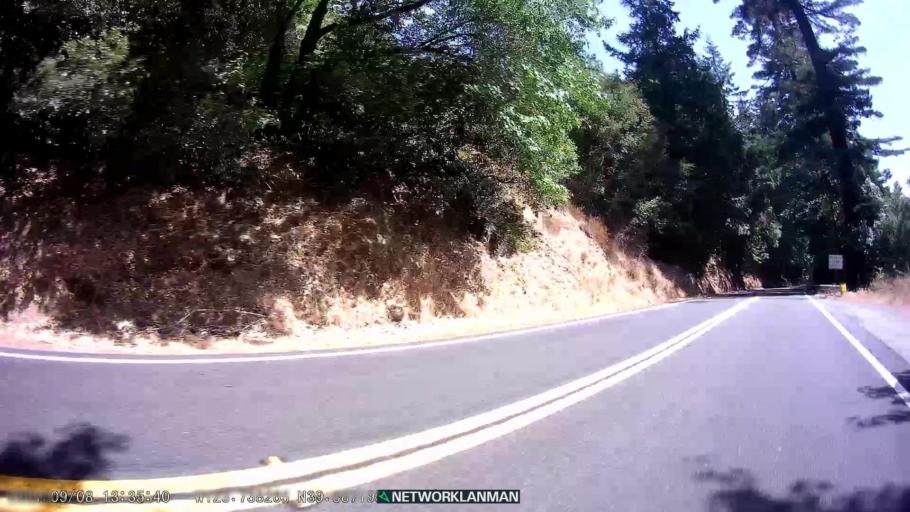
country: US
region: California
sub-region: Humboldt County
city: Redway
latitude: 39.8871
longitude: -123.7377
